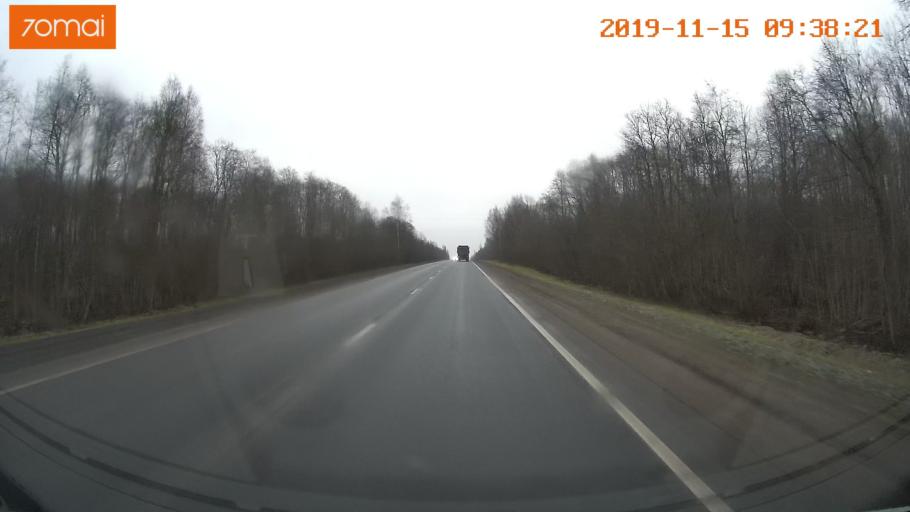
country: RU
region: Vologda
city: Sheksna
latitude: 59.2328
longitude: 38.4538
